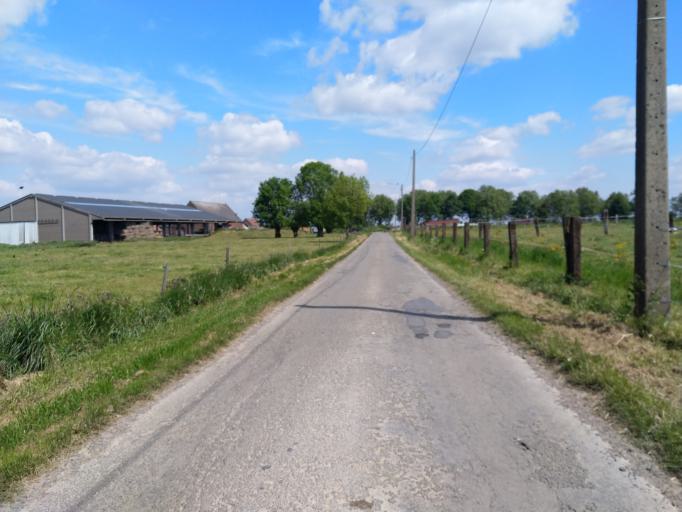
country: BE
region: Wallonia
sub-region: Province du Hainaut
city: Soignies
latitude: 50.5945
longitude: 4.0361
